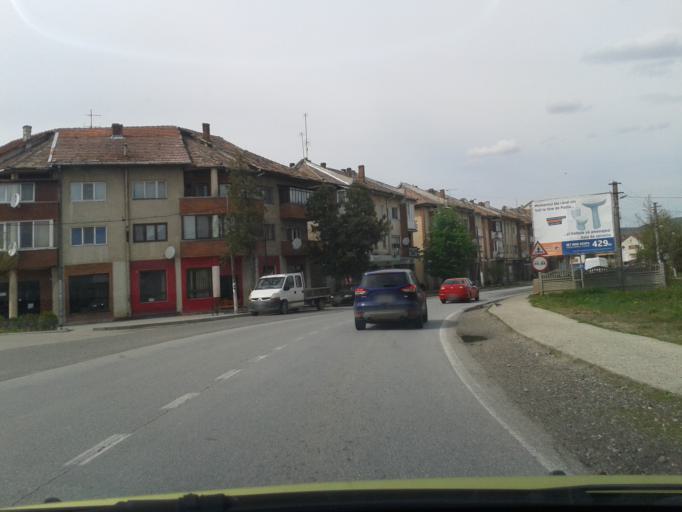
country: RO
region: Hunedoara
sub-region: Comuna Dobra
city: Dobra
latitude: 45.9119
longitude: 22.5729
